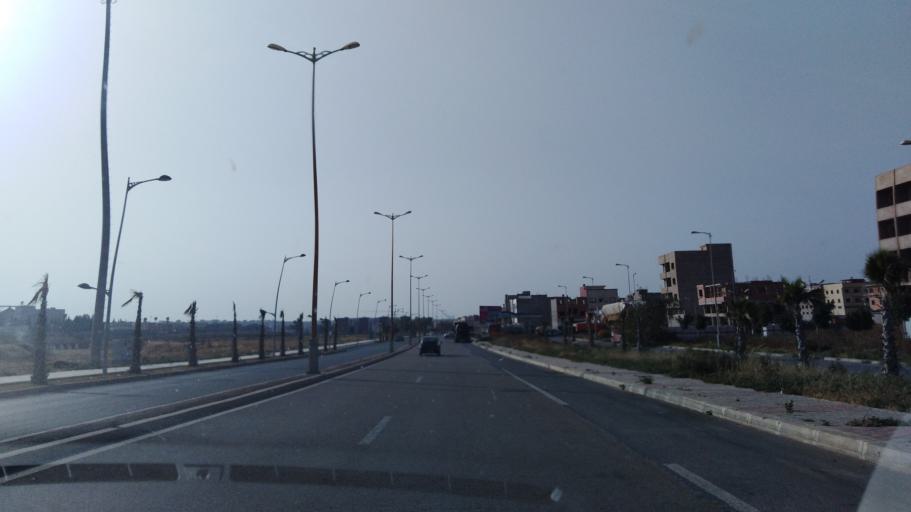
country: MA
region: Chaouia-Ouardigha
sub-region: Settat Province
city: Settat
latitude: 32.9806
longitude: -7.6067
